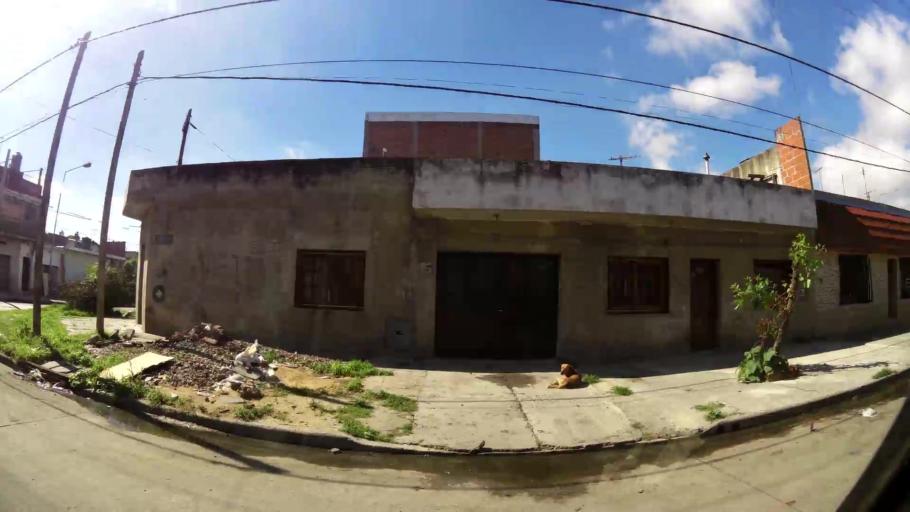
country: AR
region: Buenos Aires
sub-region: Partido de Lanus
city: Lanus
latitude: -34.6721
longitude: -58.4265
